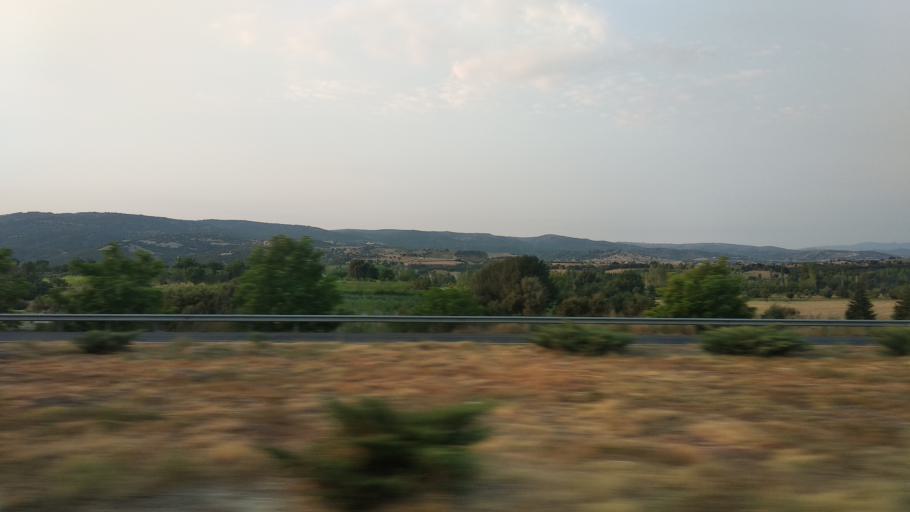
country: TR
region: Manisa
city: Selendi
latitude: 38.6218
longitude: 28.9210
